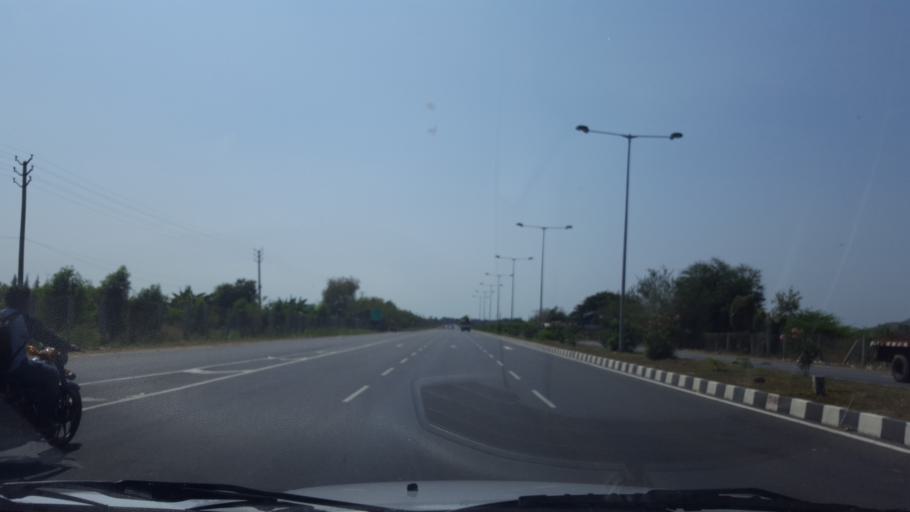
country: IN
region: Andhra Pradesh
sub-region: Prakasam
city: Addanki
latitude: 15.7518
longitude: 80.0291
